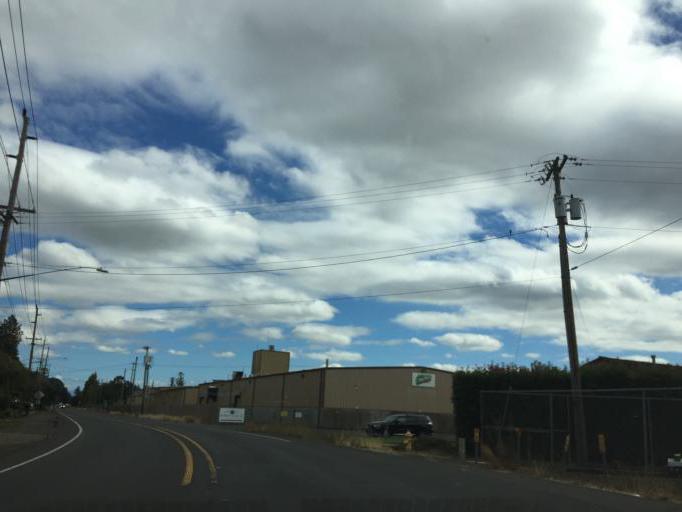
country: US
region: Oregon
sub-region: Marion County
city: Woodburn
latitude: 45.1362
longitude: -122.8419
